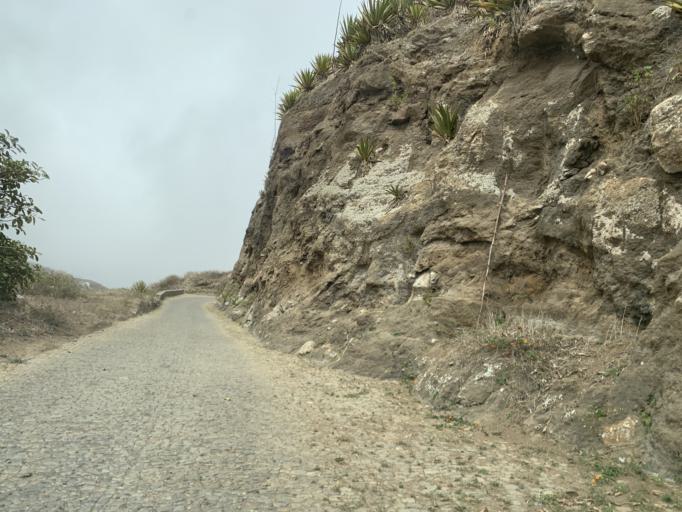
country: CV
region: Brava
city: Vila Nova Sintra
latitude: 14.8698
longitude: -24.7135
